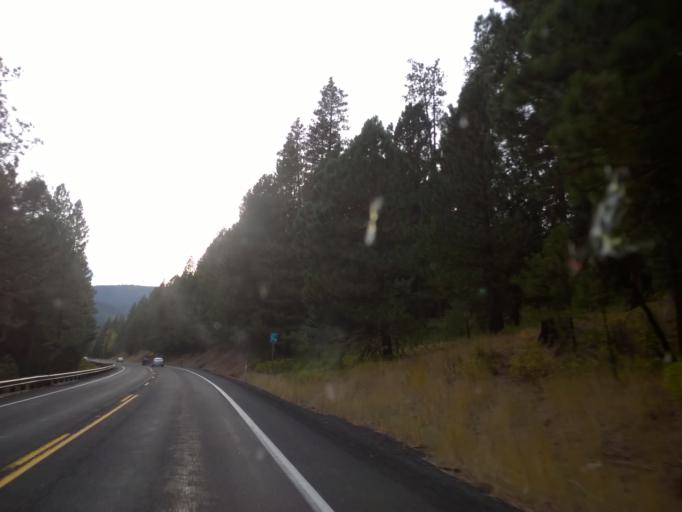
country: US
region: Washington
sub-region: Chelan County
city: Leavenworth
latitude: 47.3290
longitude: -120.6587
